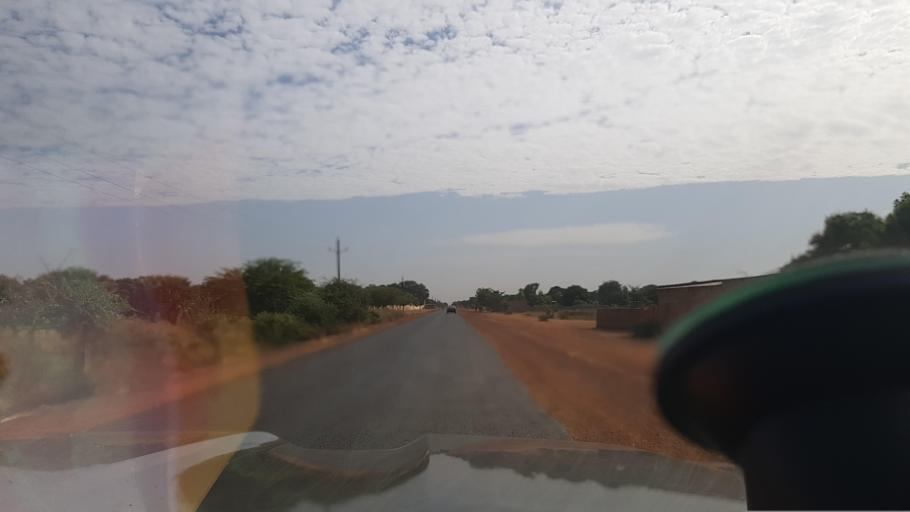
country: ML
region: Segou
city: Segou
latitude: 13.4965
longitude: -6.1657
